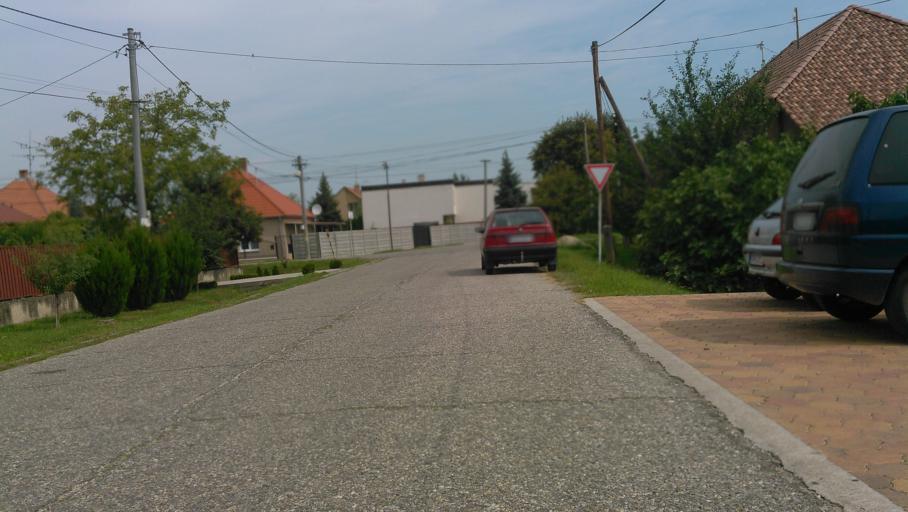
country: SK
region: Nitriansky
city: Kolarovo
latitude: 47.9088
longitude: 17.9961
